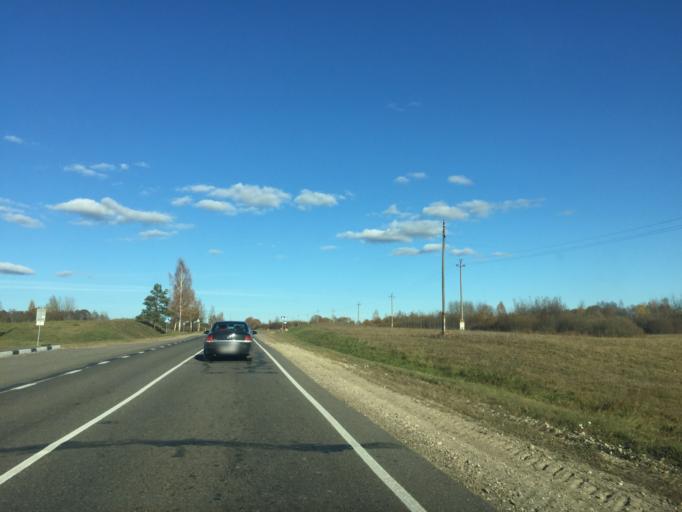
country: BY
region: Vitebsk
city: Dzisna
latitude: 55.2559
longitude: 28.1149
